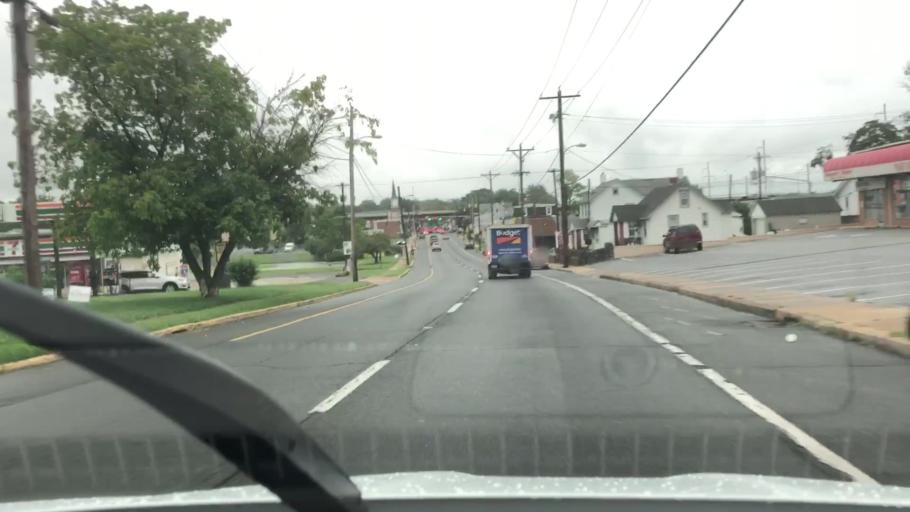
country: US
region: Delaware
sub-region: New Castle County
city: Newport
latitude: 39.7135
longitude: -75.6129
